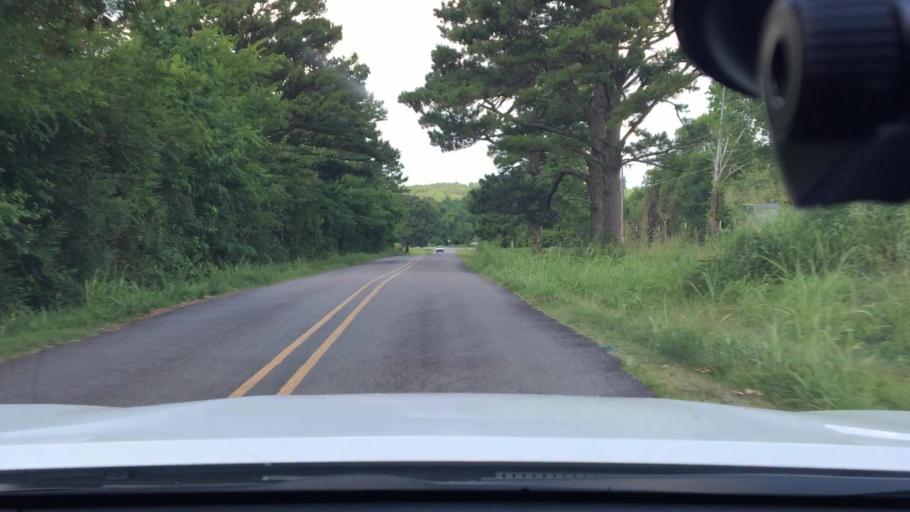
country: US
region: Arkansas
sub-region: Logan County
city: Paris
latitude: 35.2685
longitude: -93.6802
